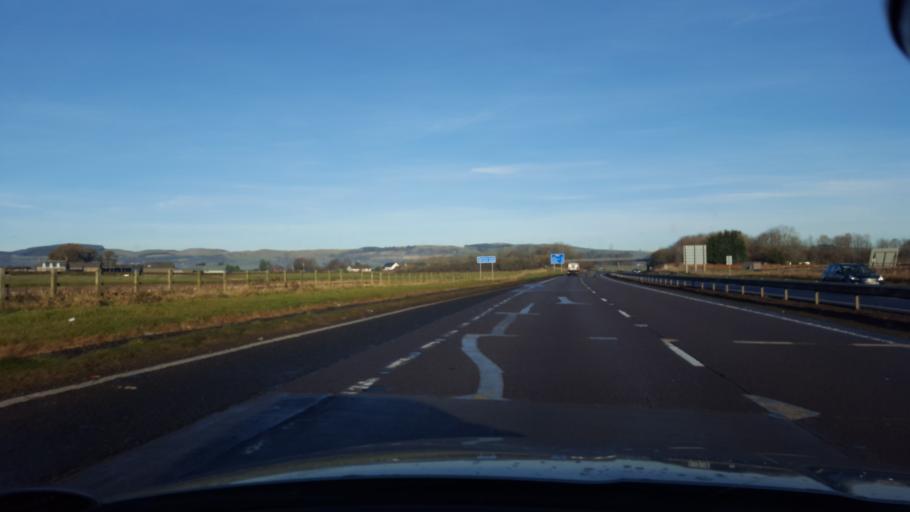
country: GB
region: Scotland
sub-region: Perth and Kinross
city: Kinross
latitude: 56.2140
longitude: -3.4378
